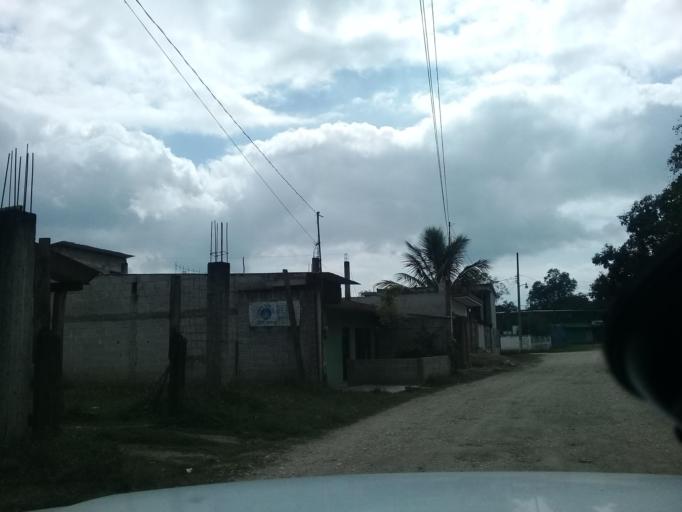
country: MX
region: Veracruz
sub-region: Xalapa
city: Fraccionamiento las Fuentes
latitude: 19.4743
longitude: -96.8796
